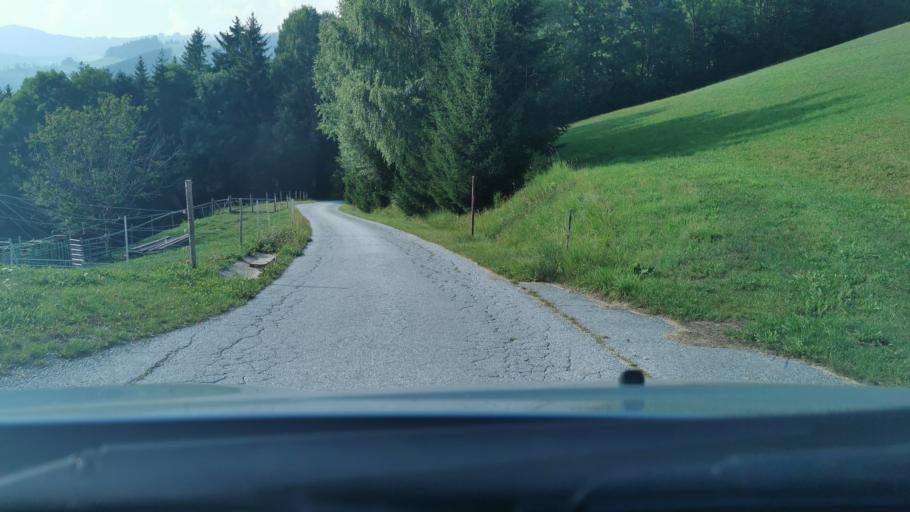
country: AT
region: Styria
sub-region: Politischer Bezirk Weiz
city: Fischbach
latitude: 47.3870
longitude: 15.6363
